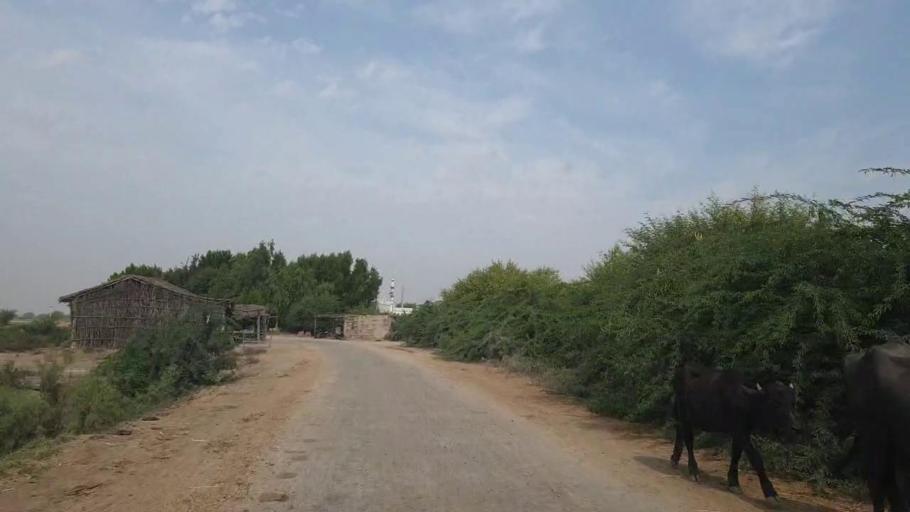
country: PK
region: Sindh
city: Rajo Khanani
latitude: 24.9367
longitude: 68.9864
